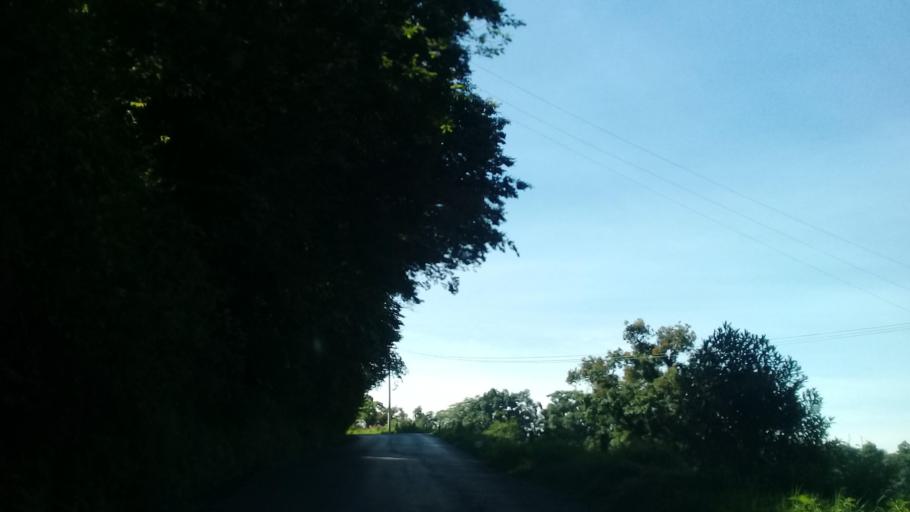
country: MX
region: Veracruz
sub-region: Tlalnelhuayocan
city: Guadalupe Victoria
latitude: 19.5292
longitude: -96.9499
